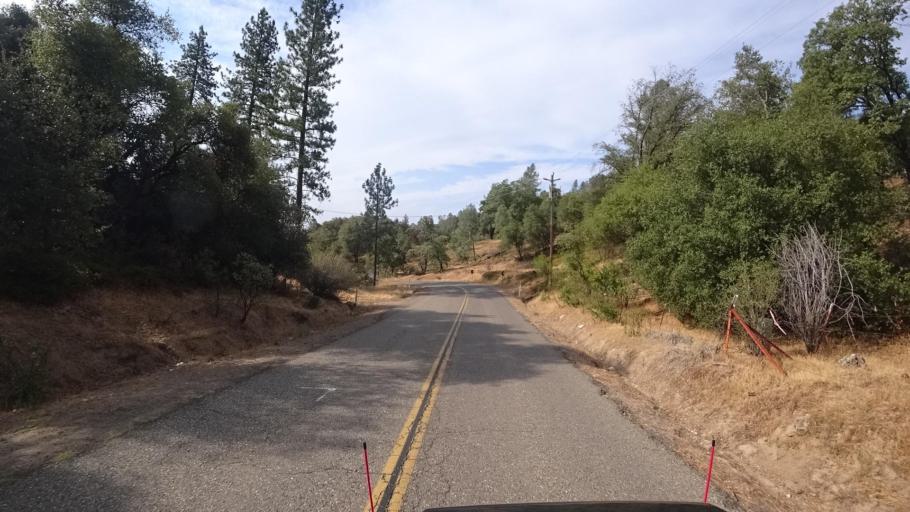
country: US
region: California
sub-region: Madera County
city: Ahwahnee
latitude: 37.4733
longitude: -119.7724
